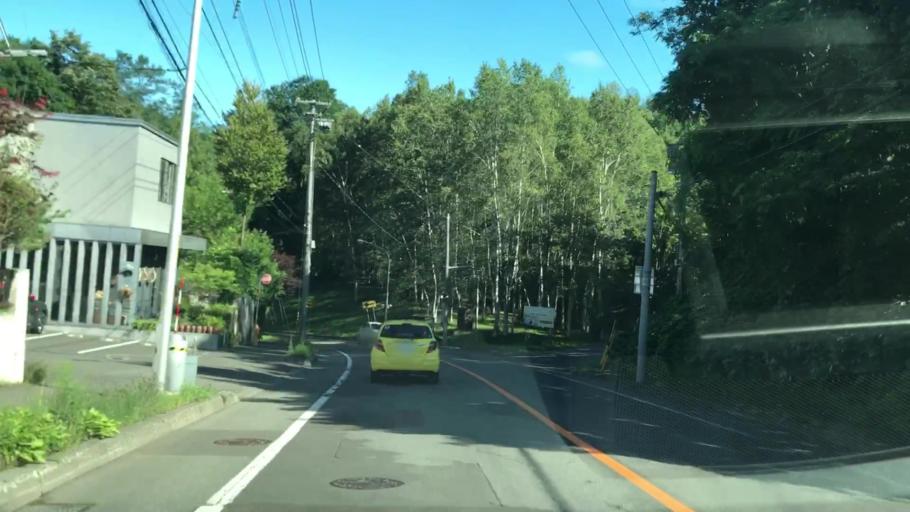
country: JP
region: Hokkaido
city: Sapporo
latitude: 43.0428
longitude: 141.3117
